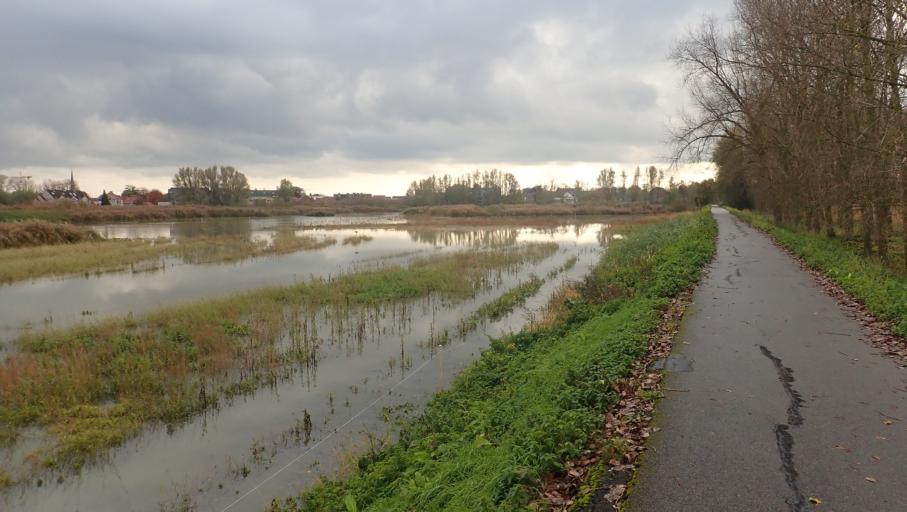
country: BE
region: Flanders
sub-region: Provincie Oost-Vlaanderen
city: Hamme
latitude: 51.1041
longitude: 4.1290
